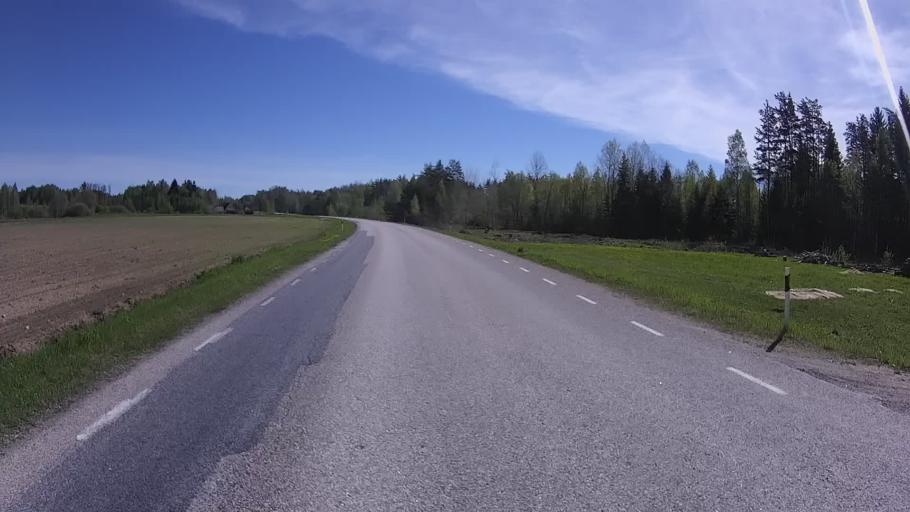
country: EE
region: Polvamaa
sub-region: Raepina vald
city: Rapina
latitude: 57.9669
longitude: 27.5431
